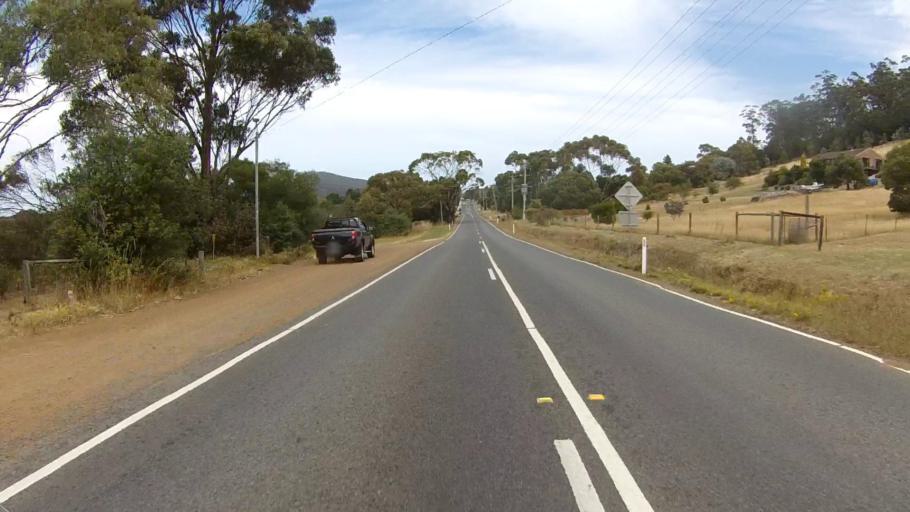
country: AU
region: Tasmania
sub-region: Clarence
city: Lauderdale
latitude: -42.9003
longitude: 147.4796
